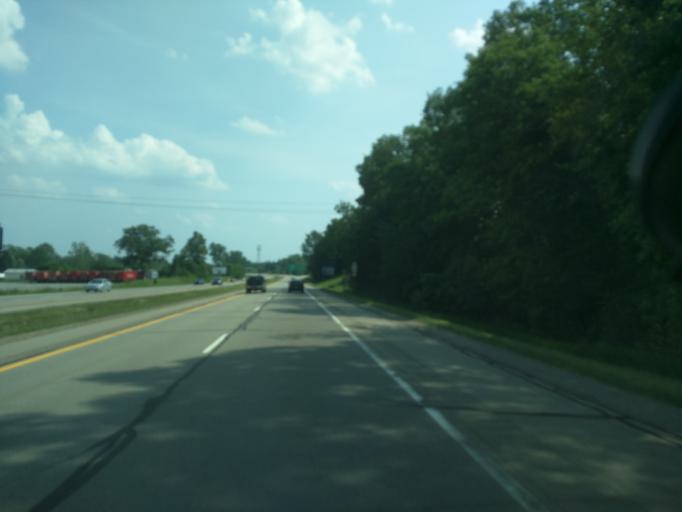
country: US
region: Michigan
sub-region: Jackson County
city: Jackson
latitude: 42.2858
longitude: -84.4329
